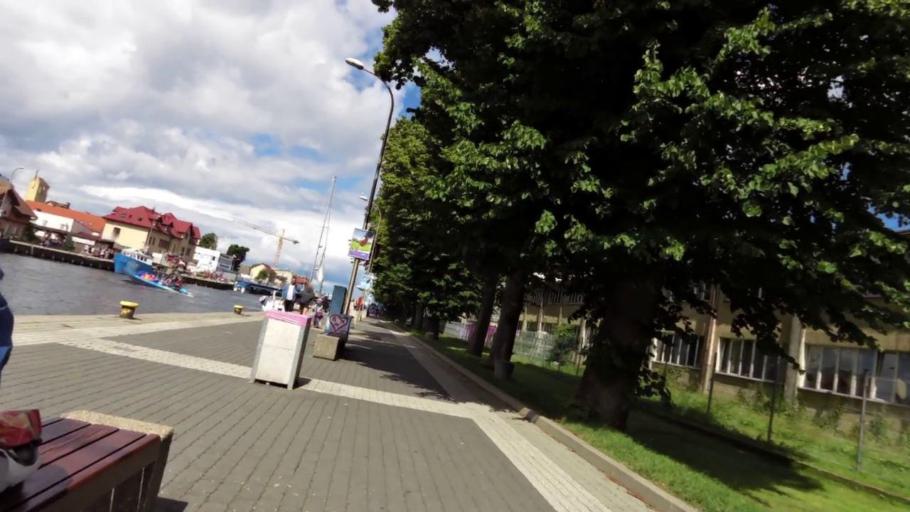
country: PL
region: West Pomeranian Voivodeship
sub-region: Powiat slawienski
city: Darlowo
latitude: 54.4388
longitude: 16.3823
